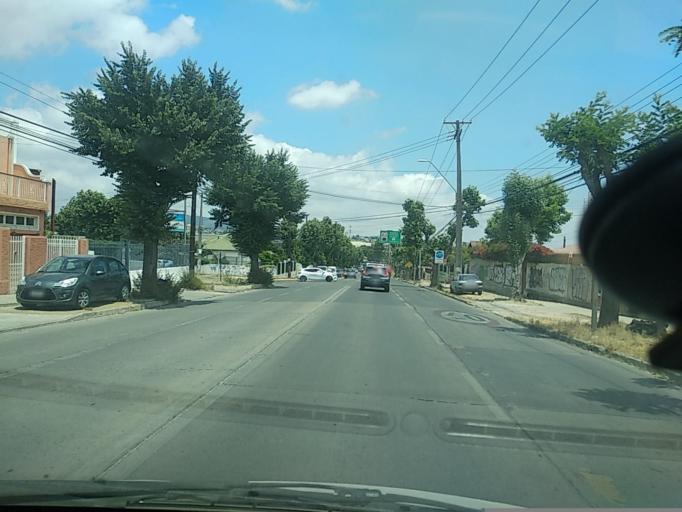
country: CL
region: Valparaiso
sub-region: Provincia de Marga Marga
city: Quilpue
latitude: -33.0437
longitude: -71.4352
